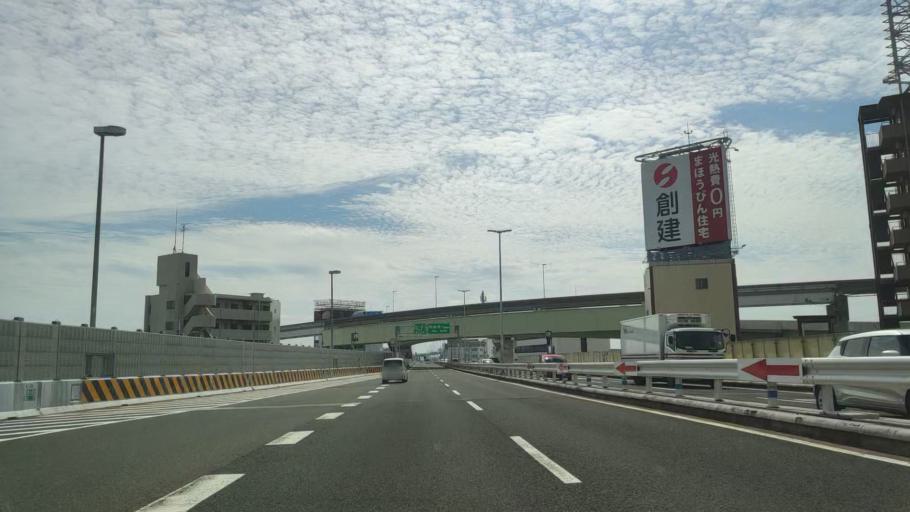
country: JP
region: Osaka
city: Toyonaka
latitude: 34.7904
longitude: 135.4466
